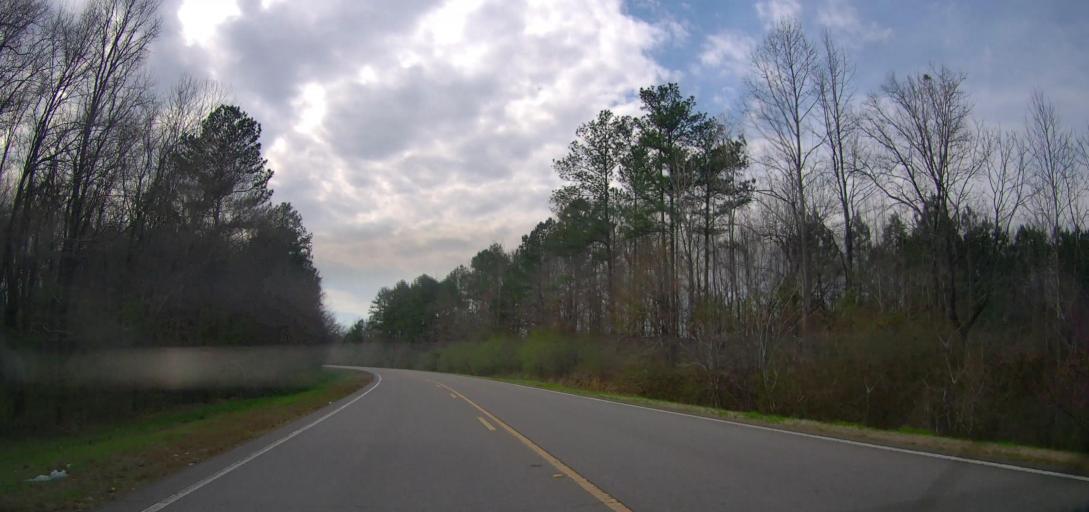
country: US
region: Alabama
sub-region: Marion County
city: Winfield
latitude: 33.9359
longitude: -87.7224
